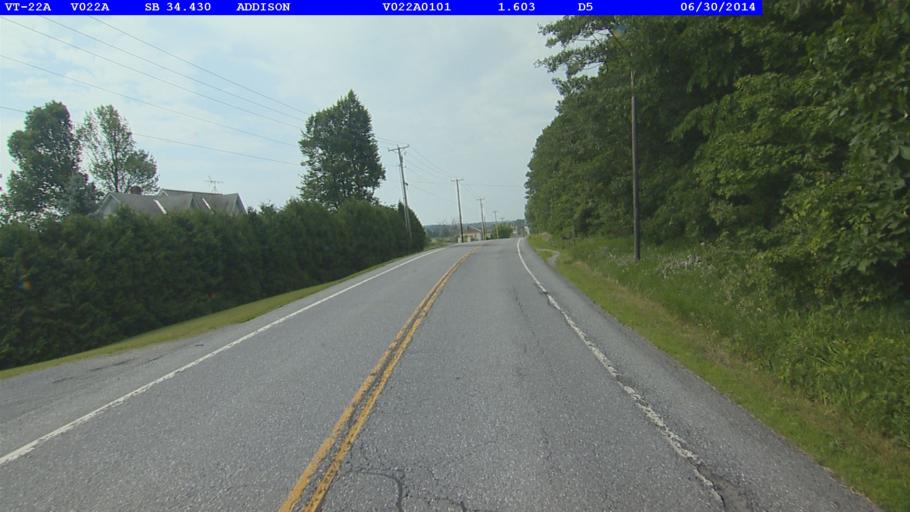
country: US
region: Vermont
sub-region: Addison County
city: Vergennes
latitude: 44.0527
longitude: -73.3013
